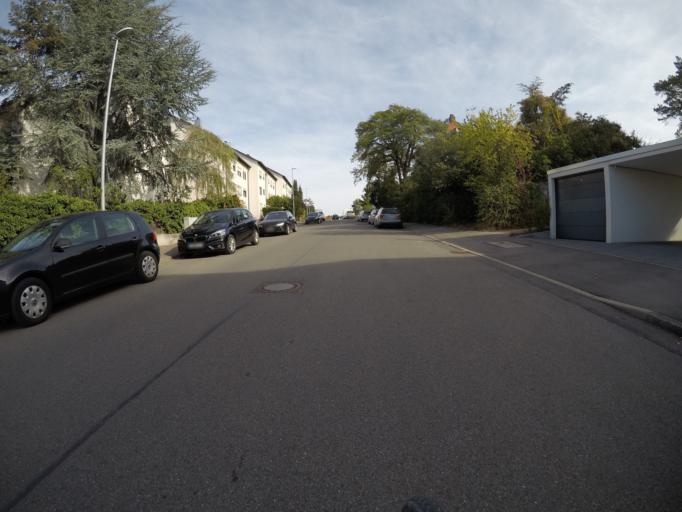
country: DE
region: Baden-Wuerttemberg
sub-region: Regierungsbezirk Stuttgart
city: Korntal
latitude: 48.8227
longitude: 9.1179
